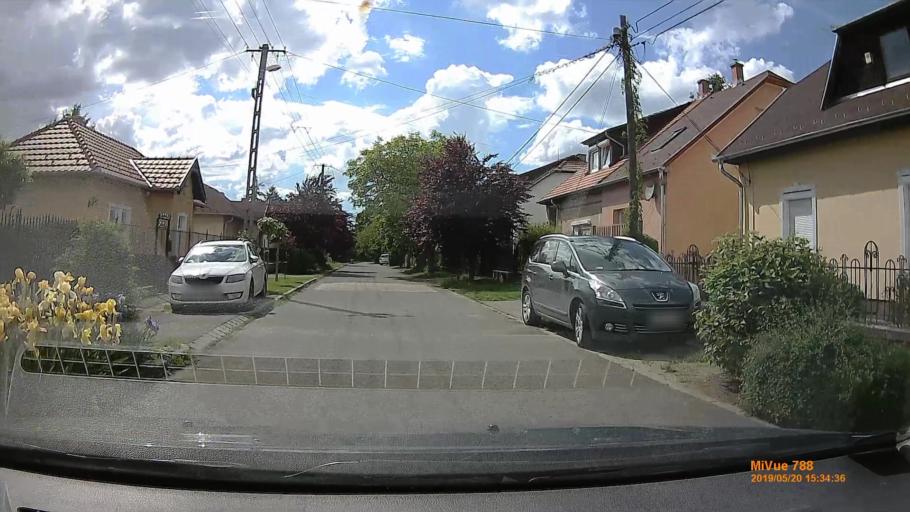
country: HU
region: Budapest
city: Budapest XVII. keruelet
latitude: 47.4894
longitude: 19.2550
